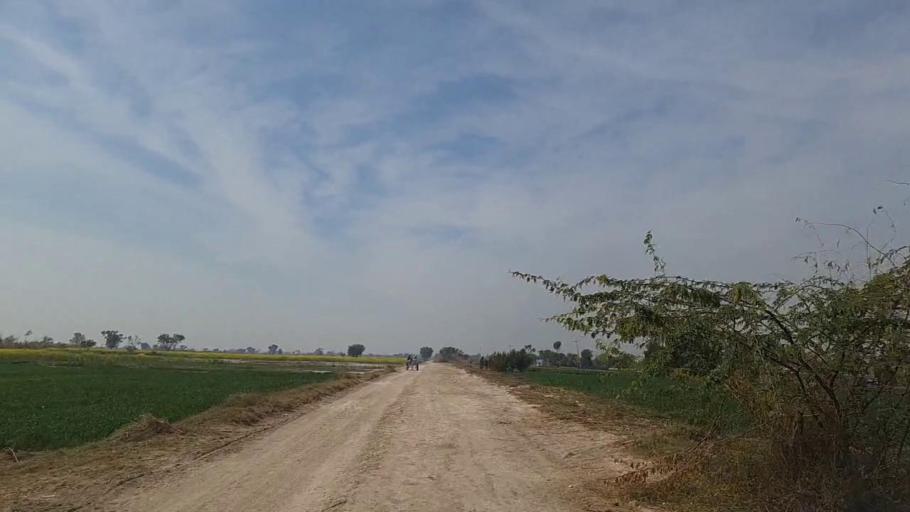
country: PK
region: Sindh
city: Nawabshah
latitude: 26.3276
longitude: 68.4326
